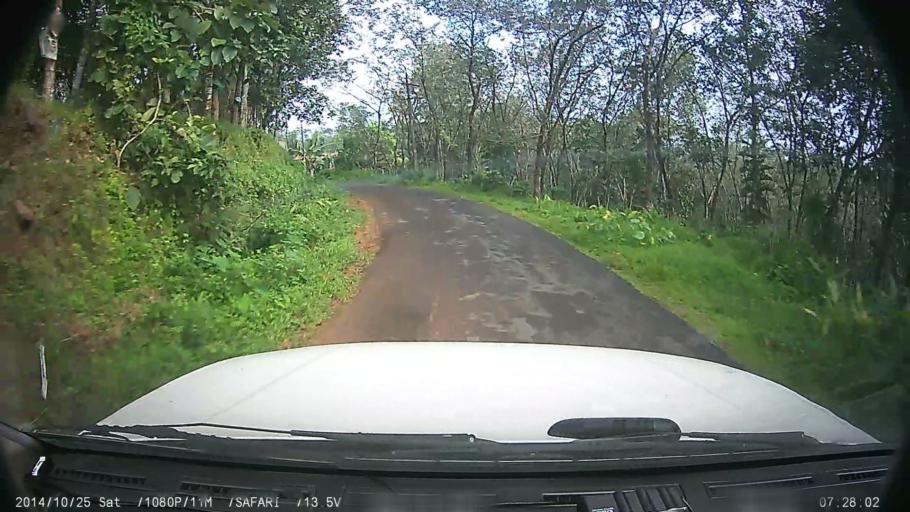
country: IN
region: Kerala
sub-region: Kottayam
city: Palackattumala
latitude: 9.7820
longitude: 76.5651
